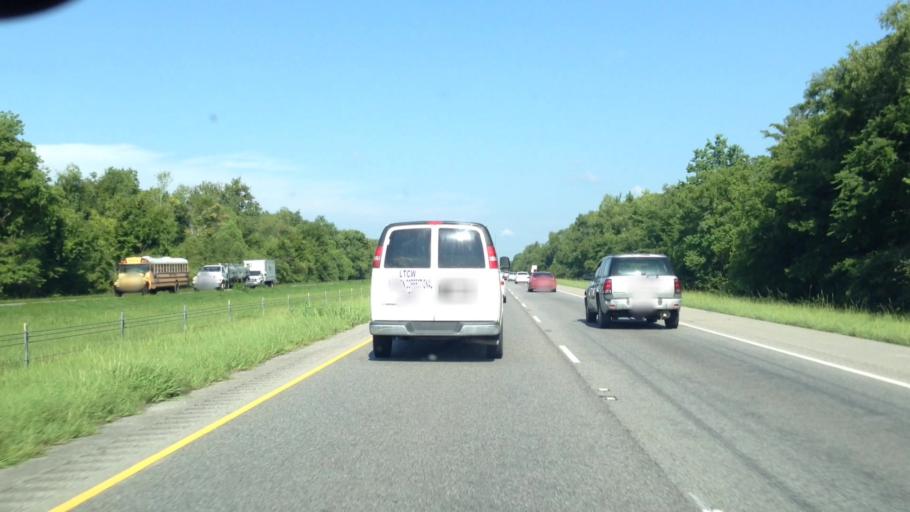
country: US
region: Louisiana
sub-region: Saint John the Baptist Parish
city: Garyville
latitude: 30.1150
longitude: -90.5875
